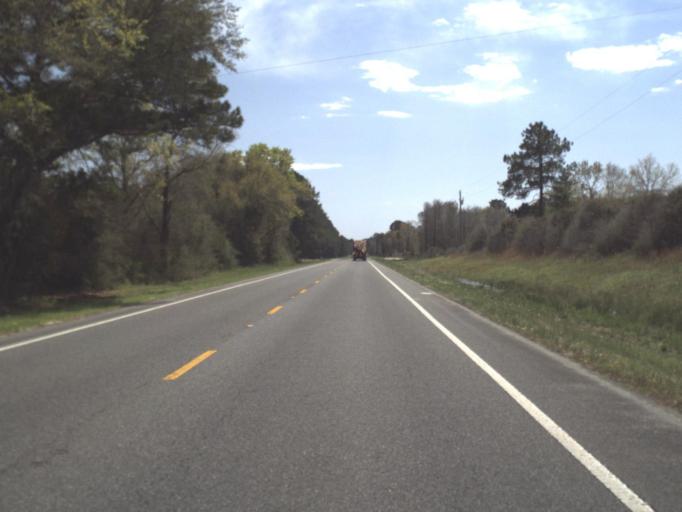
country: US
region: Florida
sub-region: Walton County
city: DeFuniak Springs
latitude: 30.8084
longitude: -85.9584
